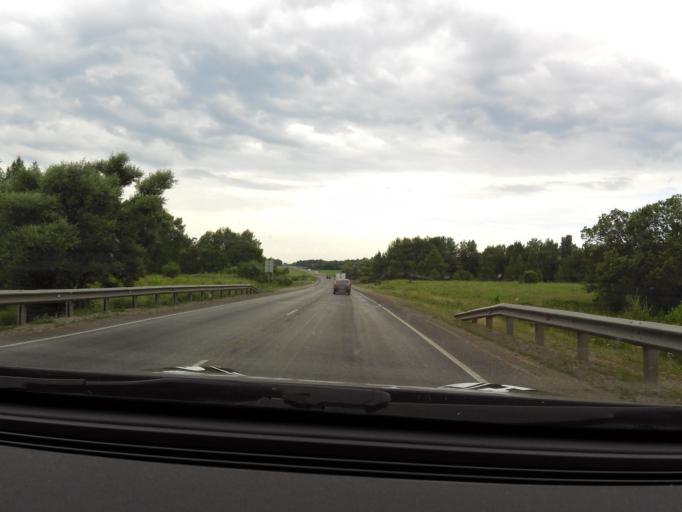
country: RU
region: Bashkortostan
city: Kudeyevskiy
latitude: 54.8166
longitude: 56.7088
